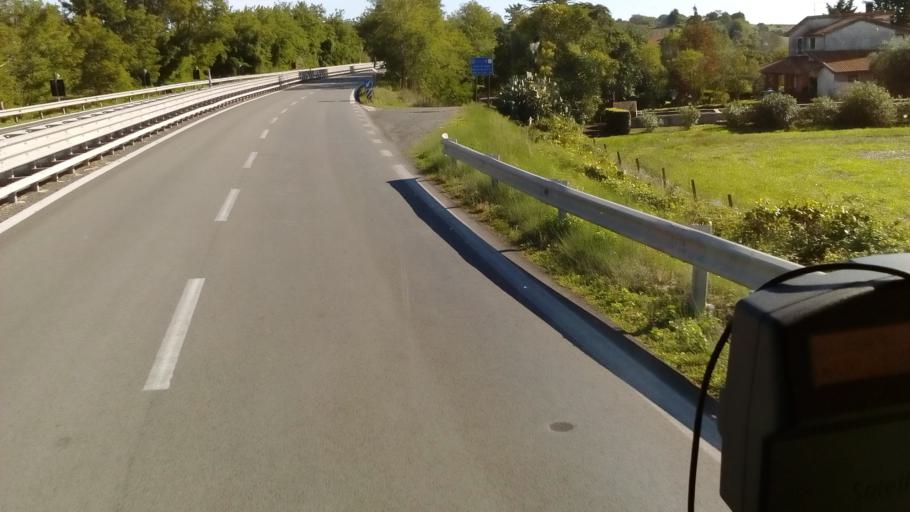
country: IT
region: Latium
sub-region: Provincia di Viterbo
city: Montalto di Castro
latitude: 42.3174
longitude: 11.6526
